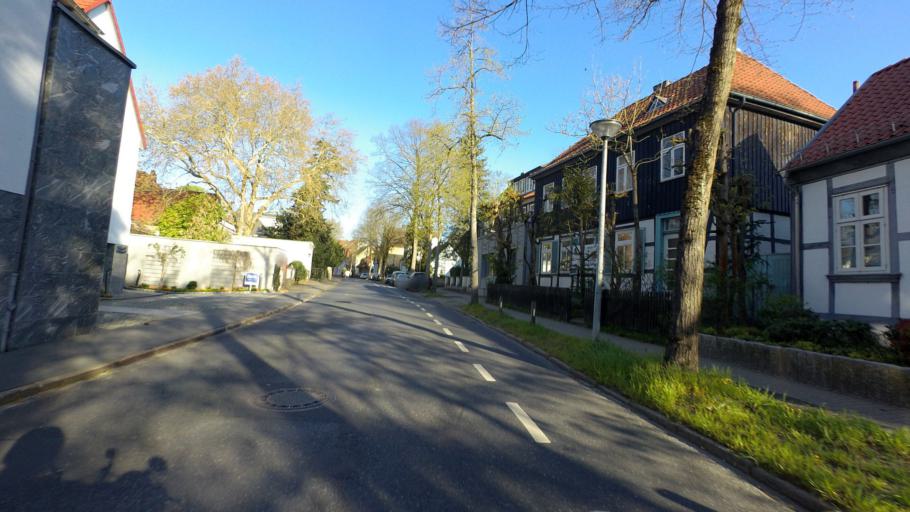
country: DE
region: Lower Saxony
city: Celle
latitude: 52.6296
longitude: 10.0747
